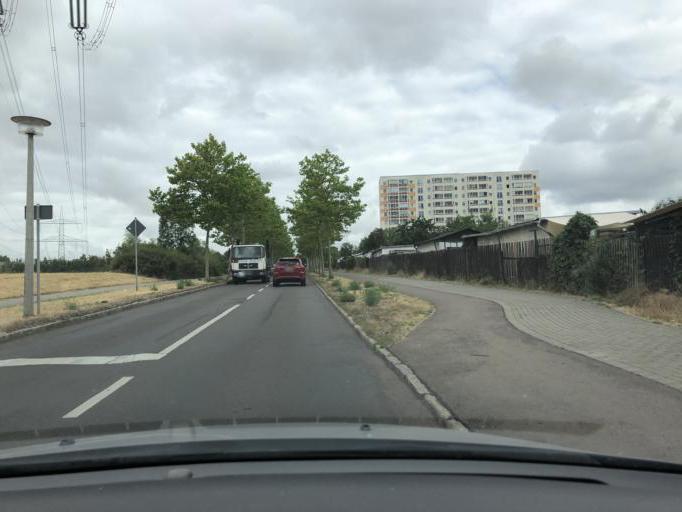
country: DE
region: Saxony-Anhalt
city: Schkopau
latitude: 51.4330
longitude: 11.9621
